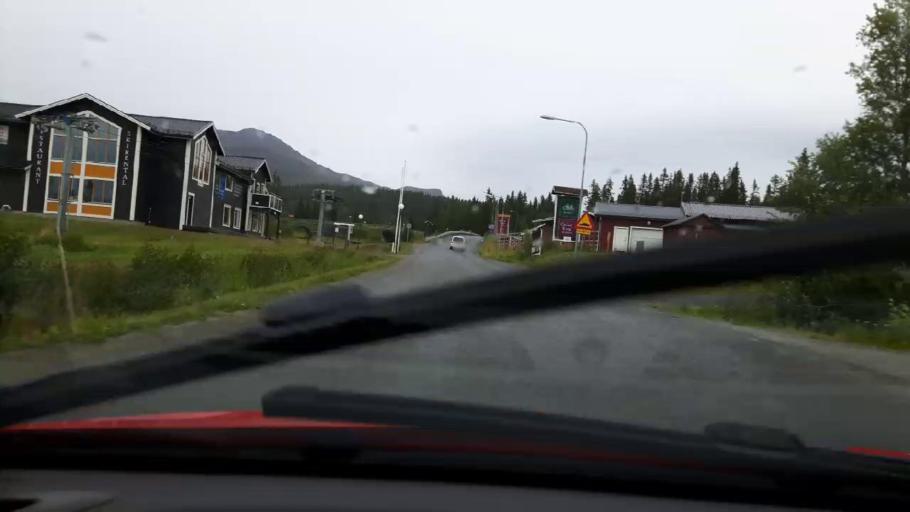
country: SE
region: Jaemtland
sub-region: Are Kommun
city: Are
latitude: 63.3879
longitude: 13.1536
